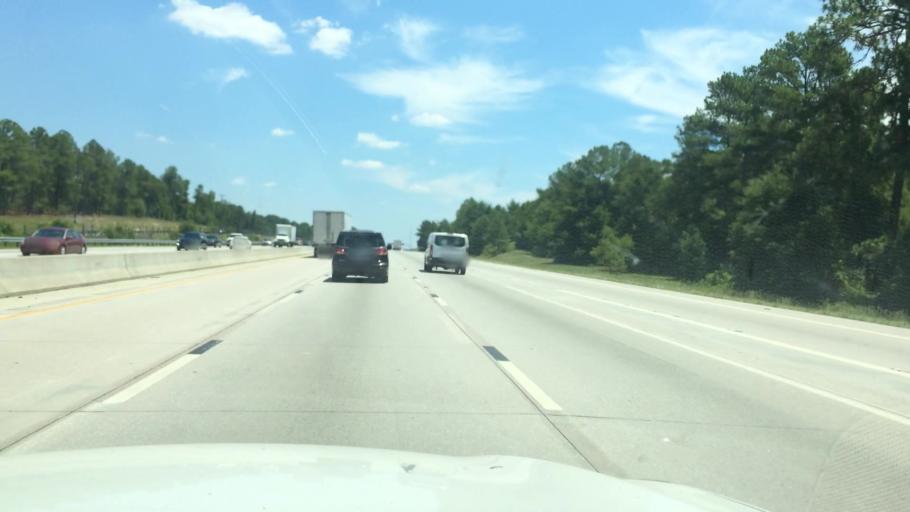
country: US
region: South Carolina
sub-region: Richland County
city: Woodfield
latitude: 34.0740
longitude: -80.9061
